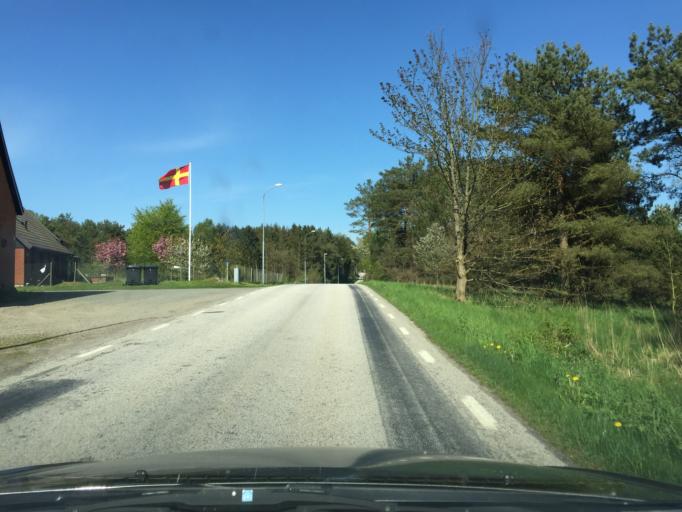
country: SE
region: Skane
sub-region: Sjobo Kommun
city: Blentarp
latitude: 55.5782
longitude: 13.5943
